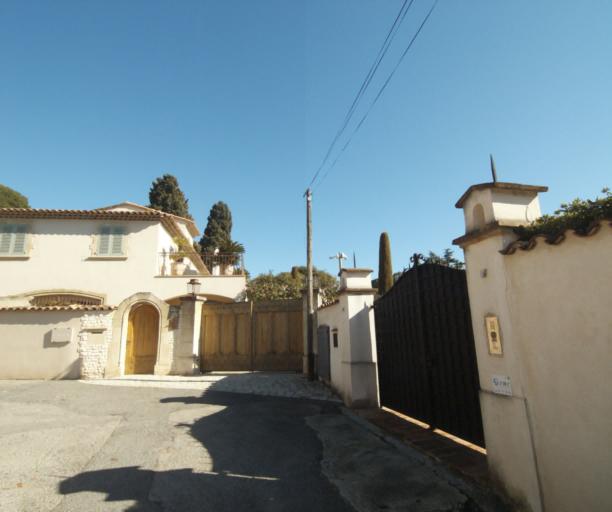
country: FR
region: Provence-Alpes-Cote d'Azur
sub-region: Departement des Alpes-Maritimes
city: Antibes
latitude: 43.5612
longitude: 7.1212
